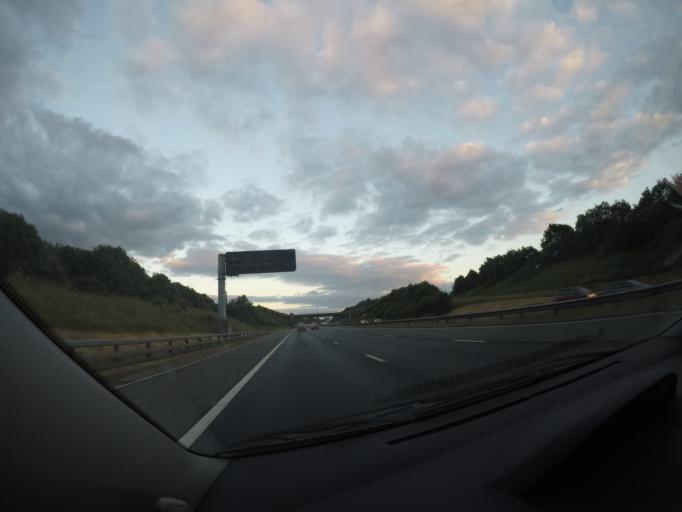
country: GB
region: England
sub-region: North Yorkshire
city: Boroughbridge
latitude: 54.0837
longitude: -1.3987
